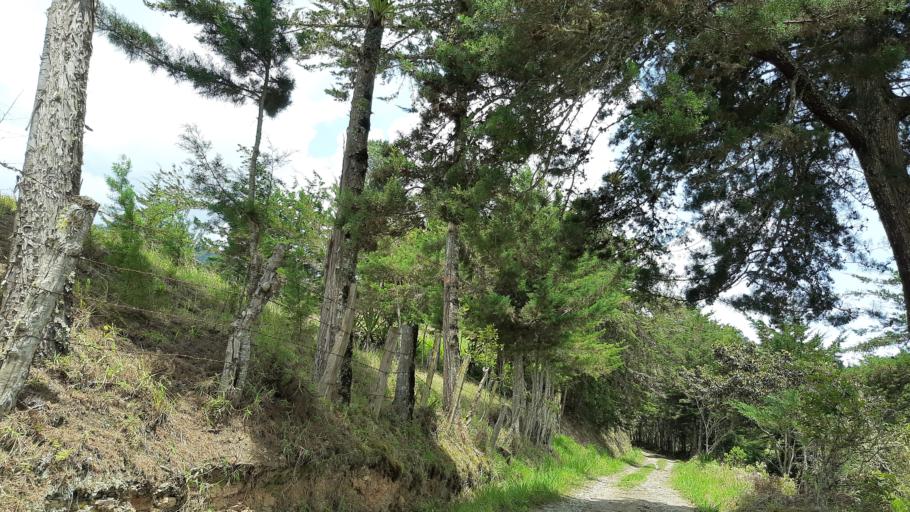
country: CO
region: Boyaca
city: Garagoa
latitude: 5.0605
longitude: -73.3556
